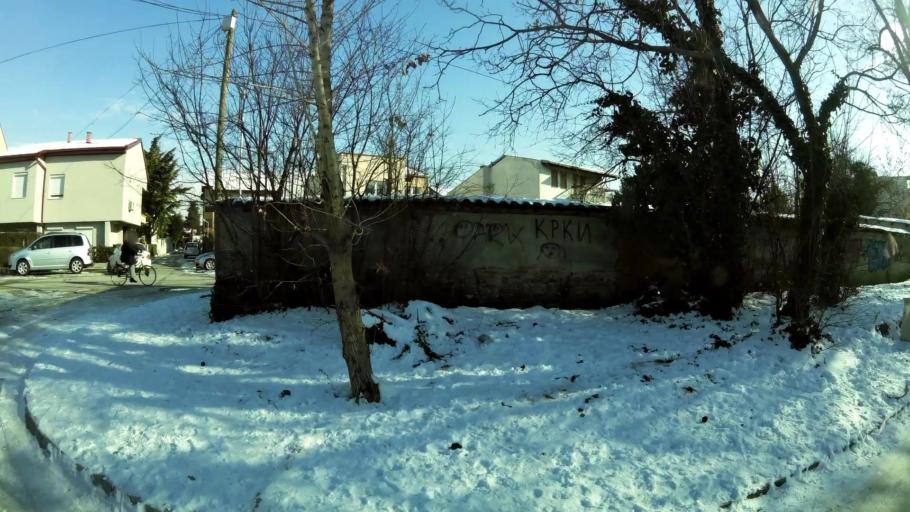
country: MK
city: Krushopek
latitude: 42.0086
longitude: 21.3733
